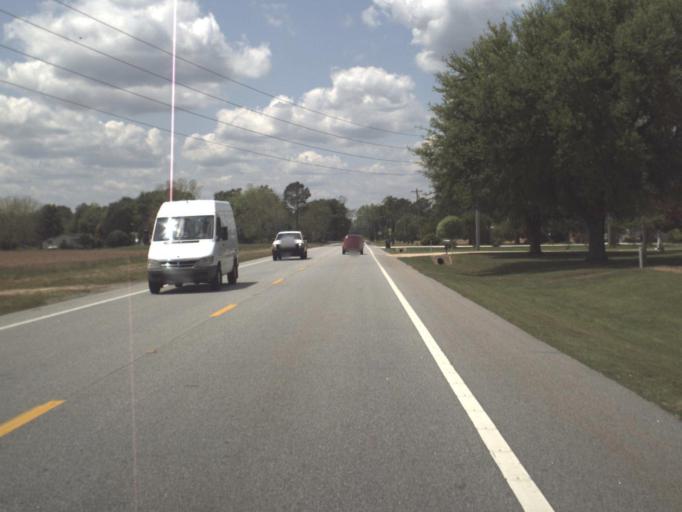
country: US
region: Alabama
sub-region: Escambia County
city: Atmore
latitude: 30.8863
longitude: -87.4544
